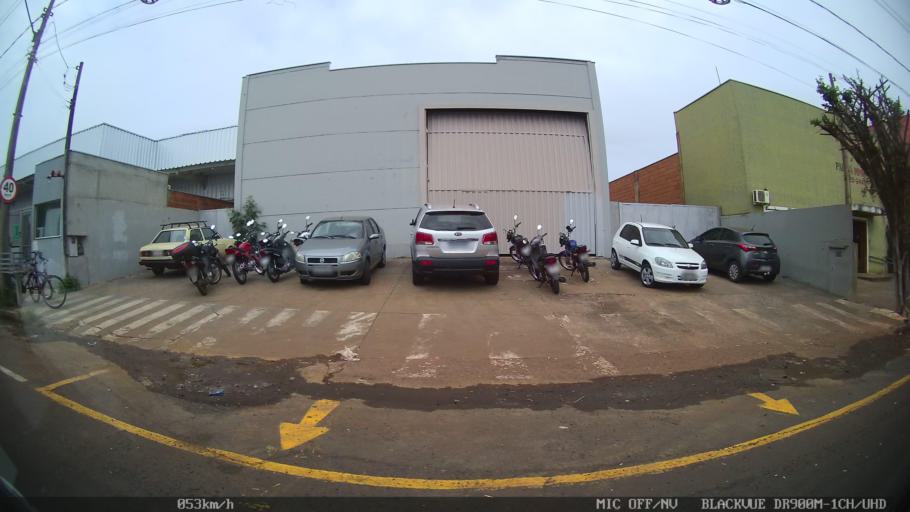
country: BR
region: Sao Paulo
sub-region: Sao Jose Do Rio Preto
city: Sao Jose do Rio Preto
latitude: -20.8266
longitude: -49.4208
